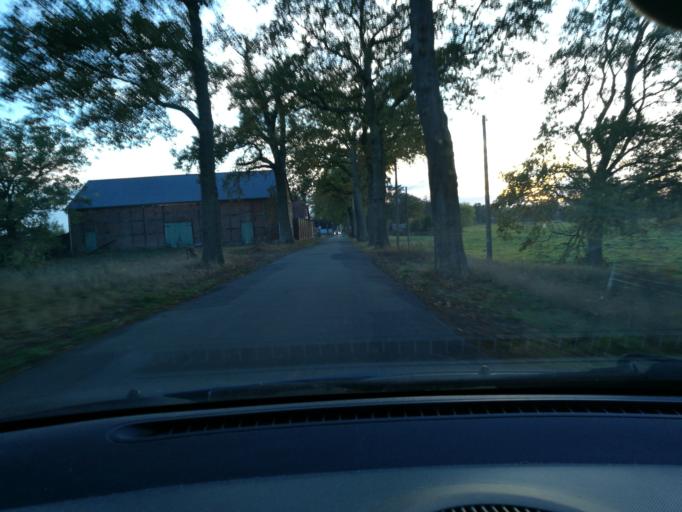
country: DE
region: Brandenburg
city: Cumlosen
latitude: 53.0842
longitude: 11.6602
